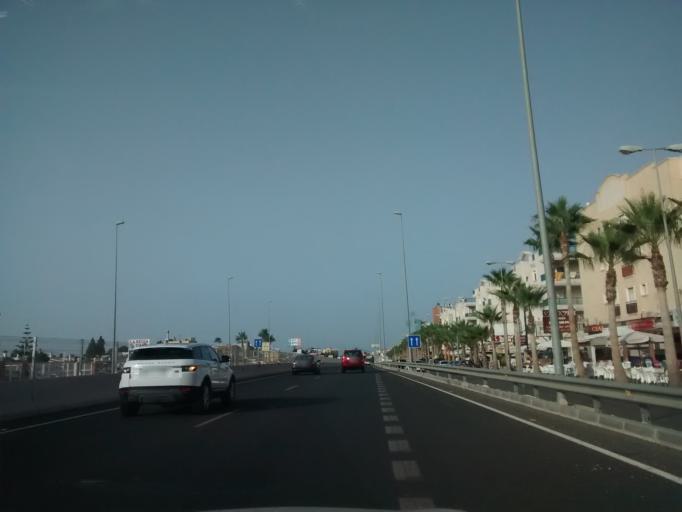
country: ES
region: Valencia
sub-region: Provincia de Alicante
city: Pilar de la Horadada
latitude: 37.9121
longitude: -0.7404
